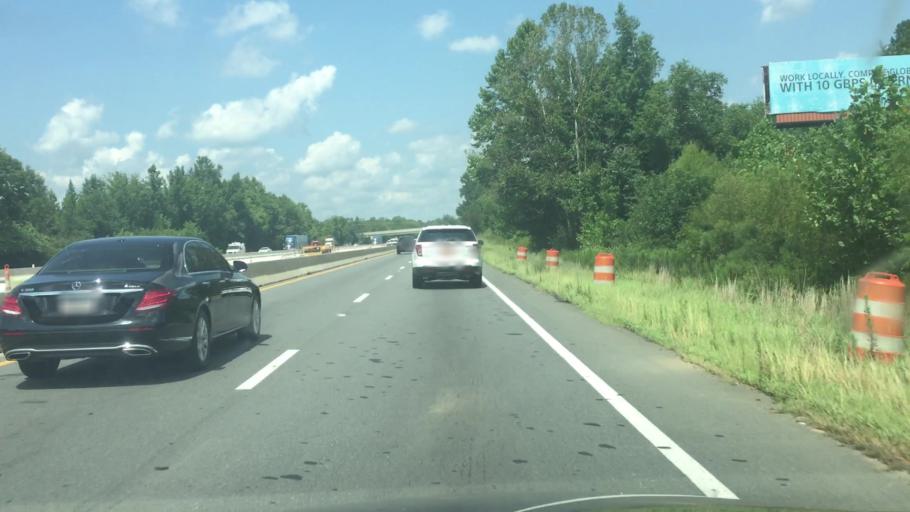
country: US
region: North Carolina
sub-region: Rowan County
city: China Grove
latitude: 35.5492
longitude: -80.5715
